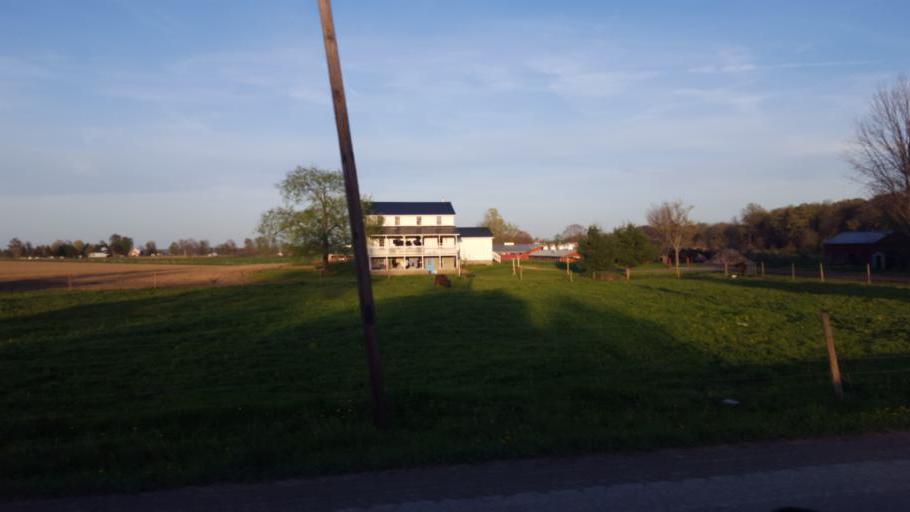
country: US
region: Ohio
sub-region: Ashtabula County
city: Andover
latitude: 41.5304
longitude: -80.5702
